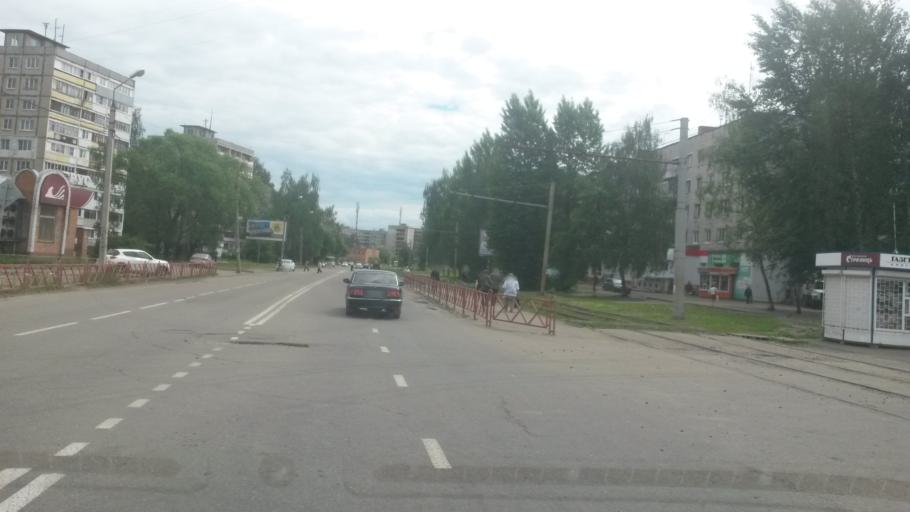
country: RU
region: Jaroslavl
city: Yaroslavl
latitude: 57.6802
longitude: 39.7801
